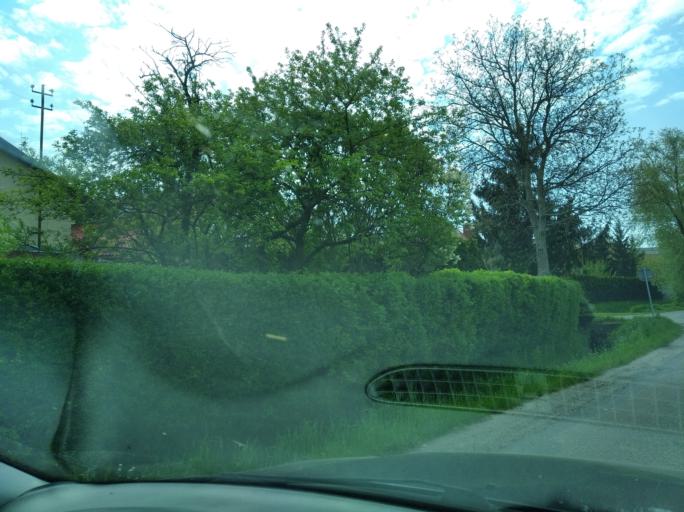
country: PL
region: Subcarpathian Voivodeship
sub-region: Powiat jaroslawski
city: Jaroslaw
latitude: 50.0145
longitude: 22.6652
